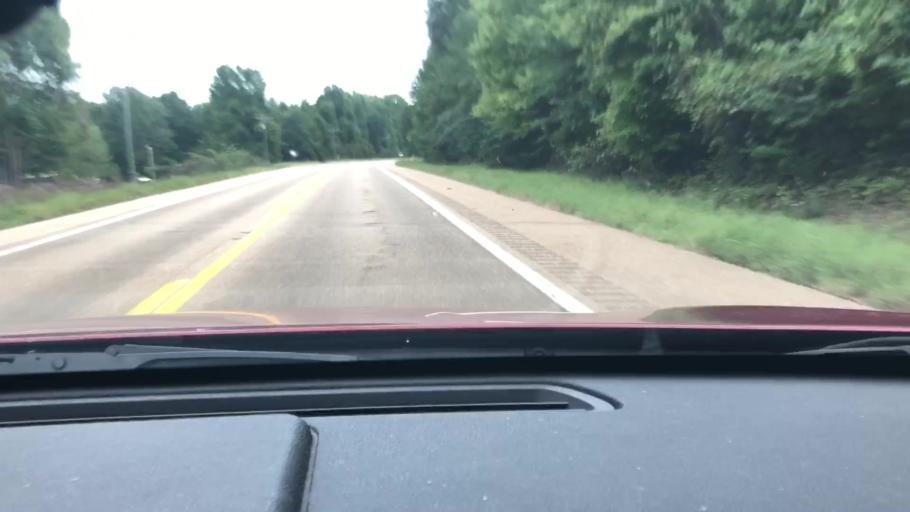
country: US
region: Arkansas
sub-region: Miller County
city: Texarkana
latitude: 33.4188
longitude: -93.8385
